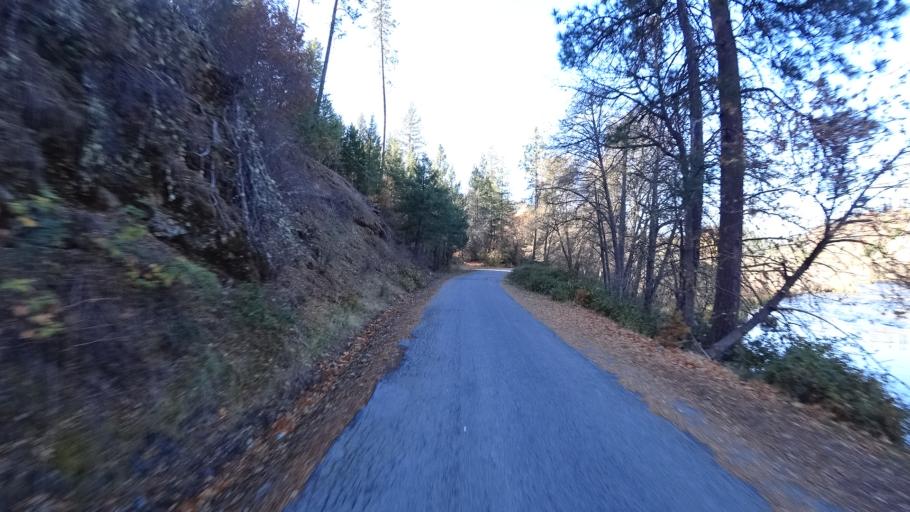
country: US
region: California
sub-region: Siskiyou County
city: Yreka
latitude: 41.8223
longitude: -122.9625
